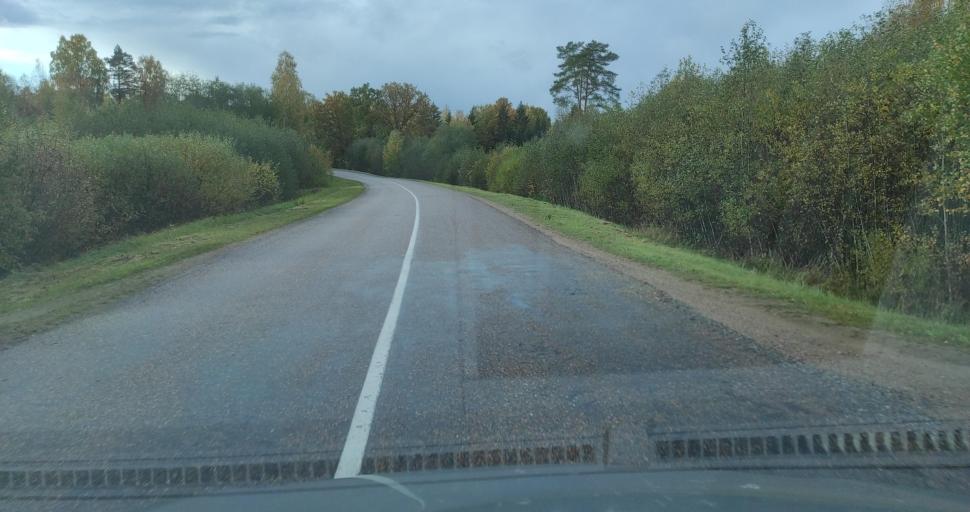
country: LV
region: Skrunda
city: Skrunda
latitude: 56.5985
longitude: 21.9044
